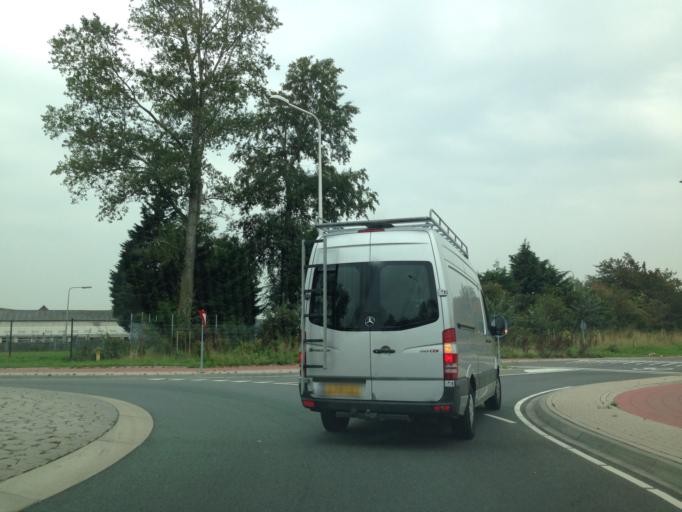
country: NL
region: South Holland
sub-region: Gemeente Westland
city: Naaldwijk
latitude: 51.9831
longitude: 4.2064
